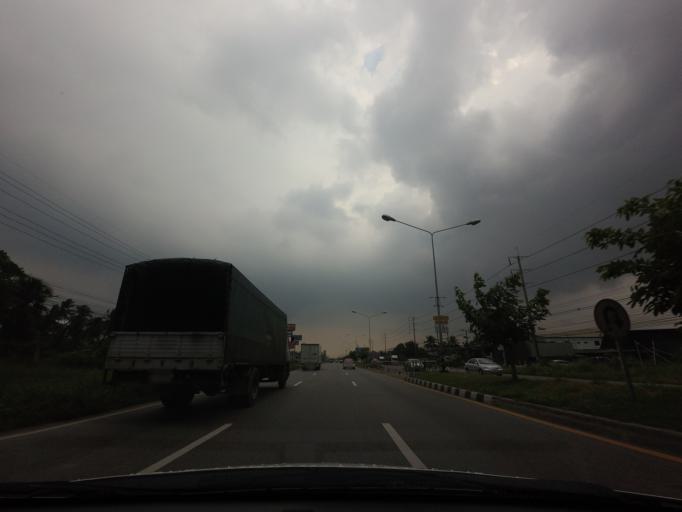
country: TH
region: Nakhon Pathom
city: Salaya
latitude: 13.7852
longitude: 100.2623
